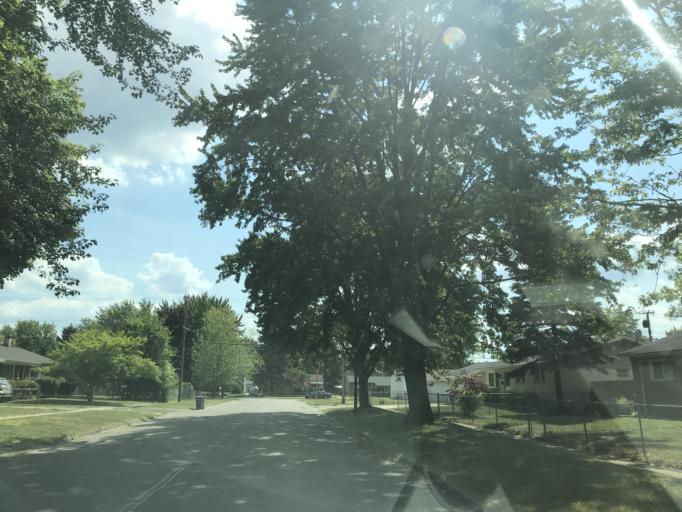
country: US
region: Michigan
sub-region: Washtenaw County
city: Ypsilanti
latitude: 42.2576
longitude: -83.5825
